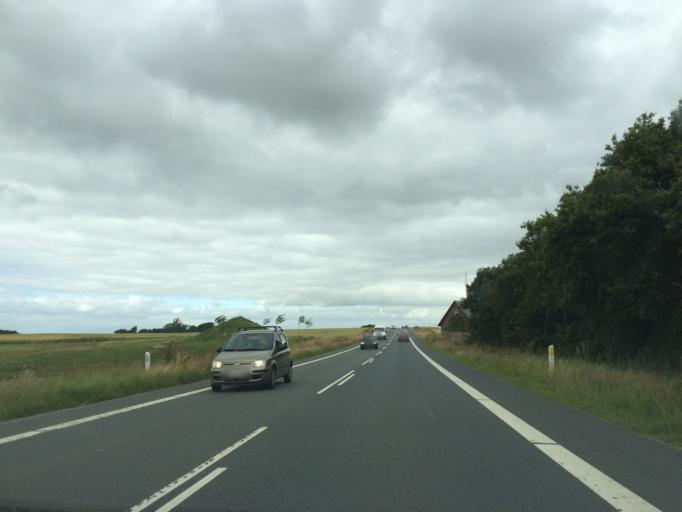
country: DK
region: Central Jutland
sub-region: Silkeborg Kommune
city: Silkeborg
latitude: 56.2049
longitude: 9.6023
